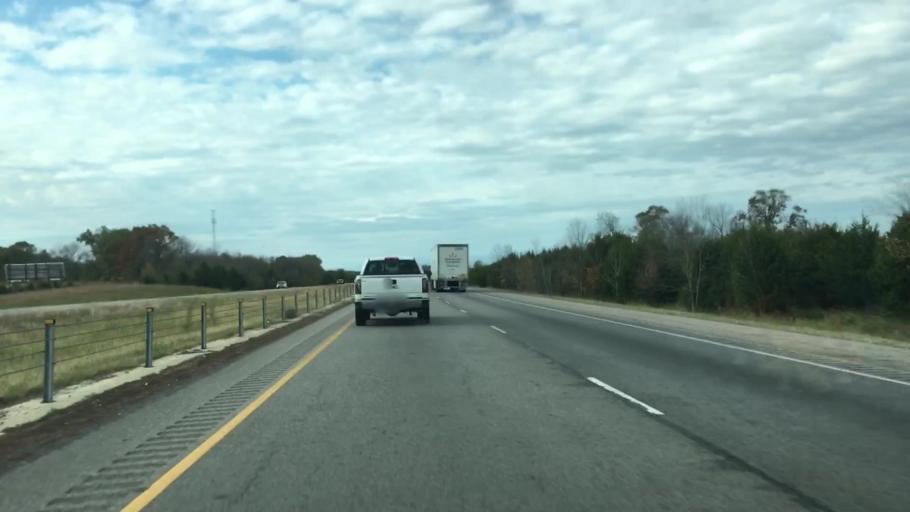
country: US
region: Arkansas
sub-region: Conway County
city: Morrilton
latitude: 35.2001
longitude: -92.8052
